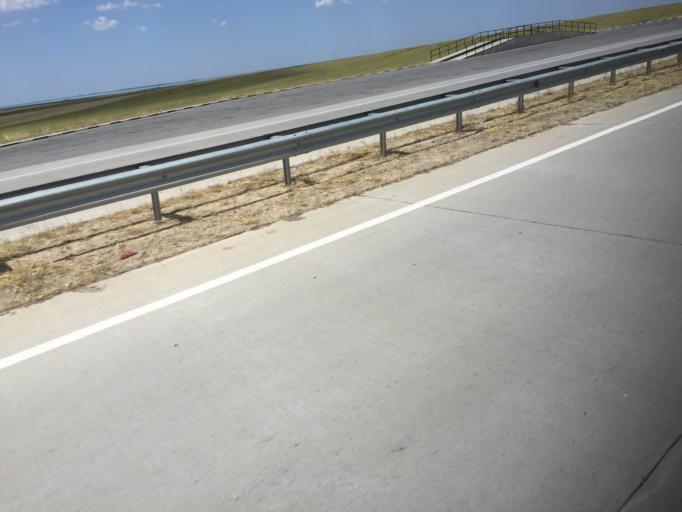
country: KZ
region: Ongtustik Qazaqstan
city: Temirlanovka
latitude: 42.7107
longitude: 69.2079
